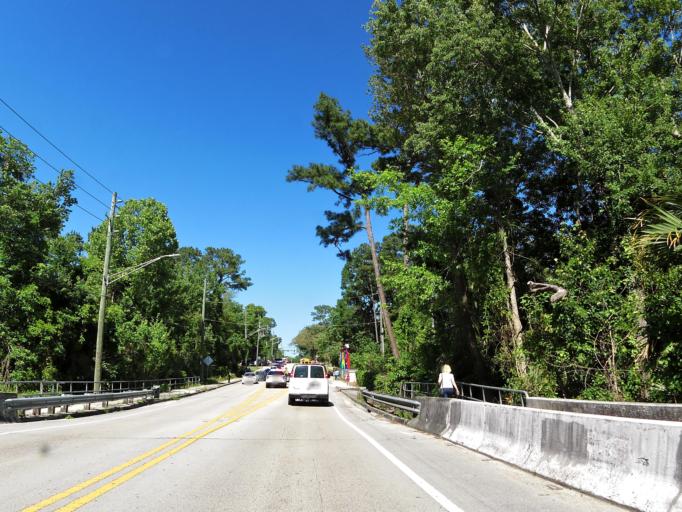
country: US
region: Florida
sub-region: Duval County
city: Jacksonville
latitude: 30.3350
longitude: -81.5807
